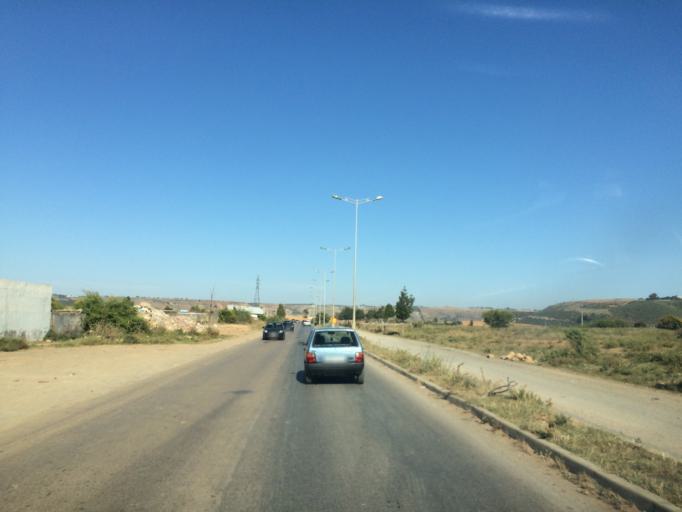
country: MA
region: Rabat-Sale-Zemmour-Zaer
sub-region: Rabat
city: Rabat
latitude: 33.9910
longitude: -6.7995
